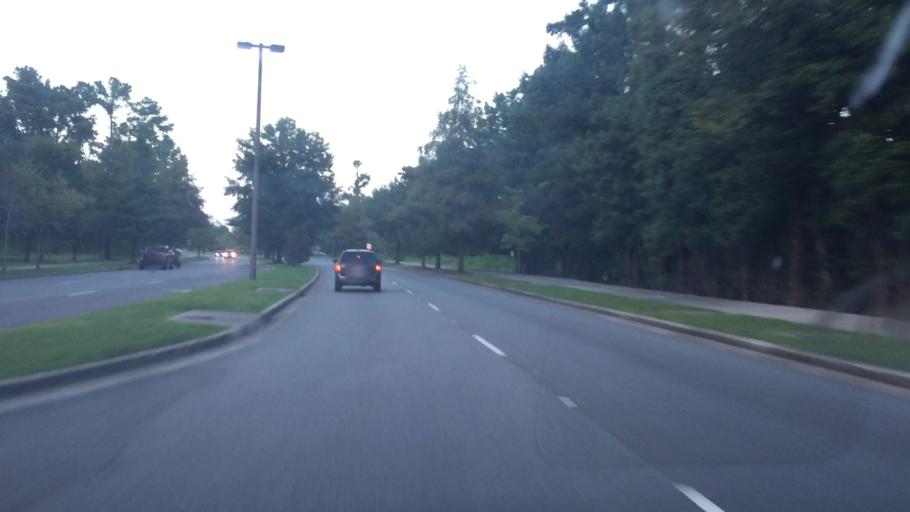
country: US
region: South Carolina
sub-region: Horry County
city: Myrtle Beach
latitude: 33.7059
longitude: -78.8867
